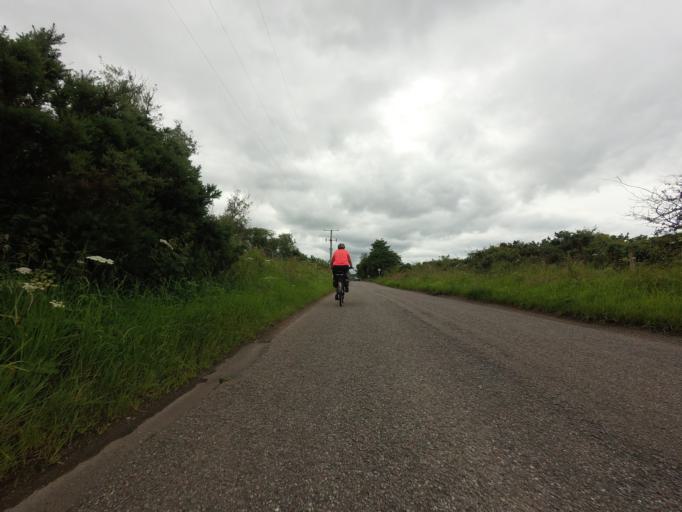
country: GB
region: Scotland
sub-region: Highland
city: Nairn
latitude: 57.5891
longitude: -3.8480
